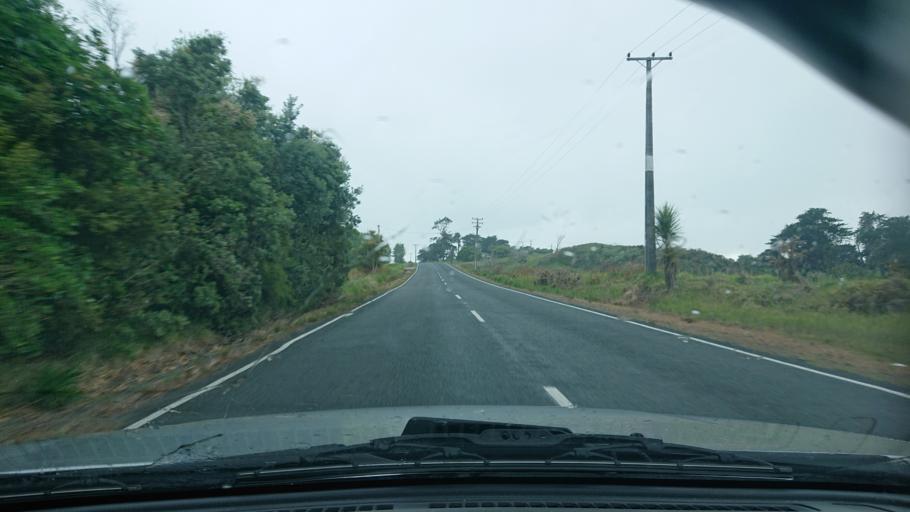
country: NZ
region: Auckland
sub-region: Auckland
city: Wellsford
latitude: -36.3291
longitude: 174.4066
